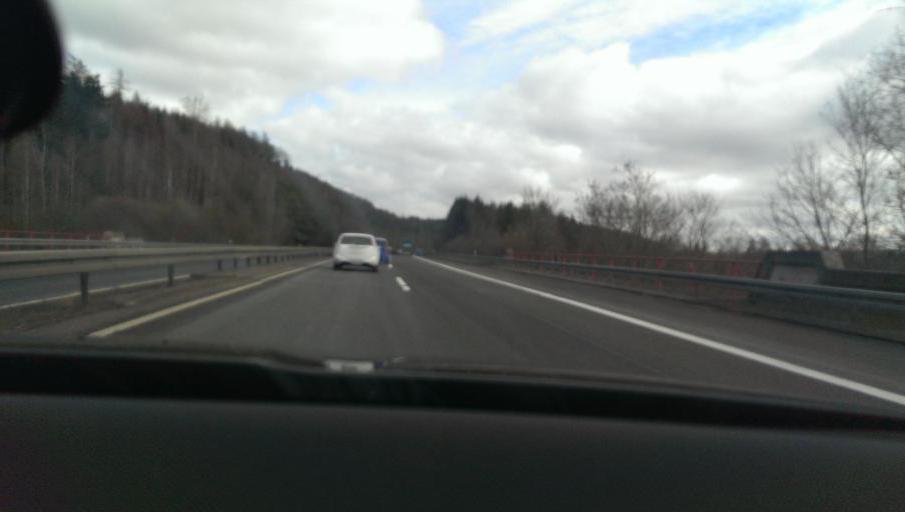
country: DE
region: Hesse
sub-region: Regierungsbezirk Darmstadt
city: Bad Soden-Salmunster
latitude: 50.3029
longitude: 9.3972
